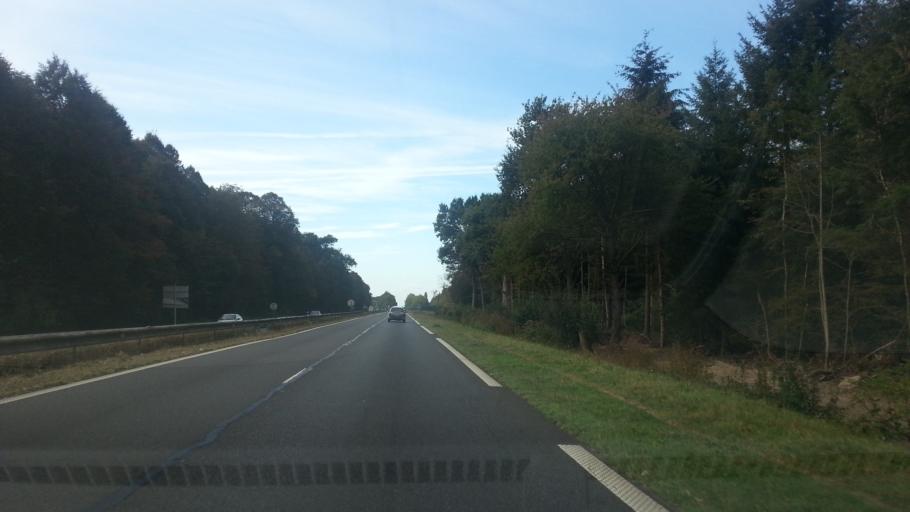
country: FR
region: Picardie
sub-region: Departement de l'Oise
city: Verneuil-en-Halatte
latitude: 49.2391
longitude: 2.5229
